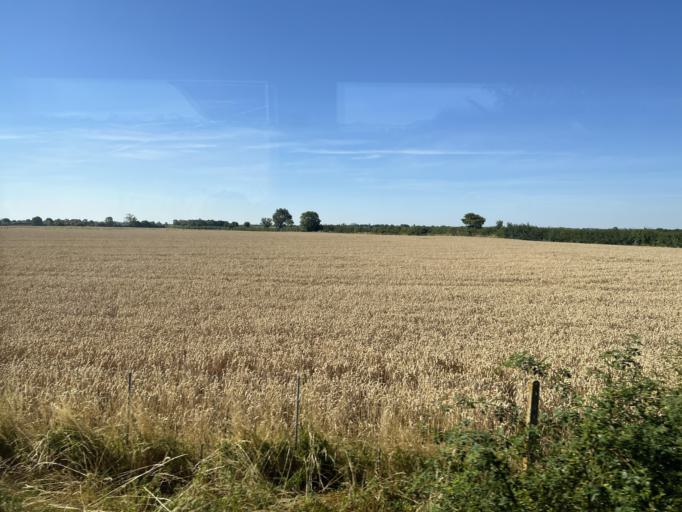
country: GB
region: England
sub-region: Lincolnshire
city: Heckington
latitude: 52.9827
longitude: -0.3219
